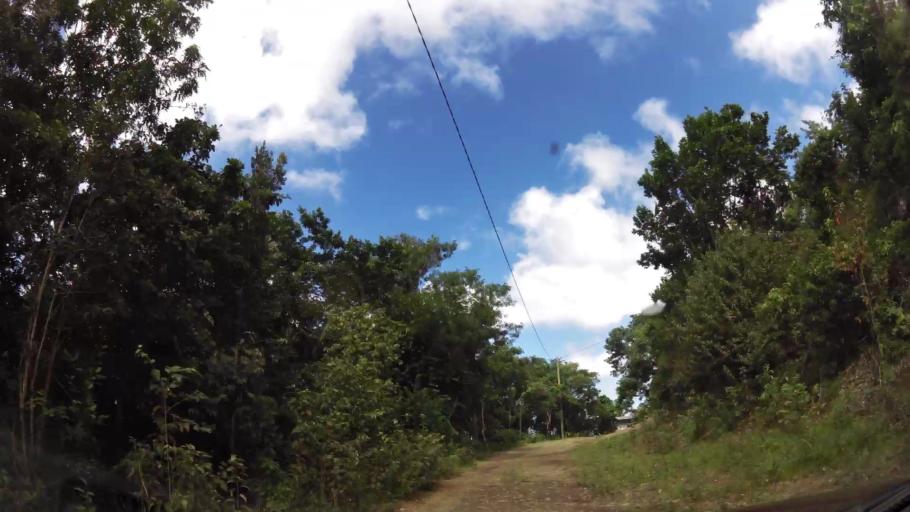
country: DM
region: Saint John
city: Portsmouth
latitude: 15.6365
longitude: -61.4578
